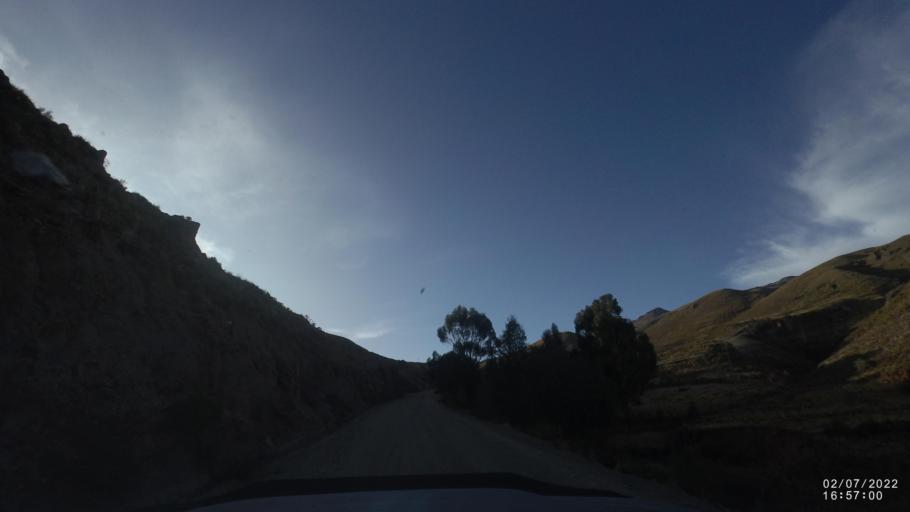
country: BO
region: Cochabamba
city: Irpa Irpa
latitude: -17.9525
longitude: -66.5449
